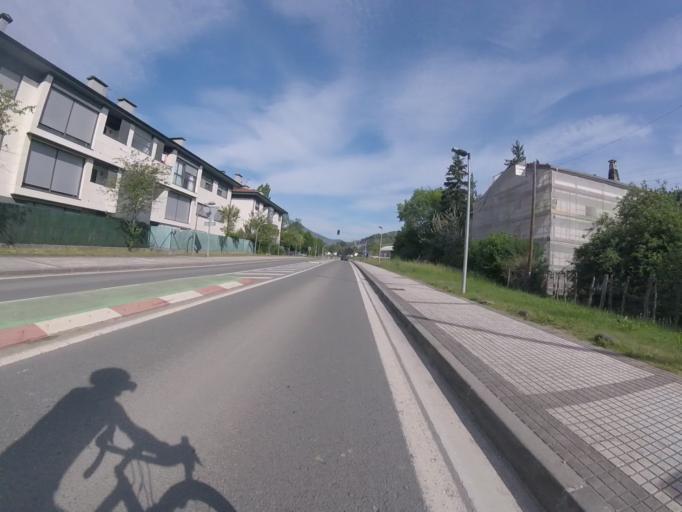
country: ES
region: Basque Country
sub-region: Provincia de Guipuzcoa
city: Gabiria
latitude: 43.0653
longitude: -2.2770
